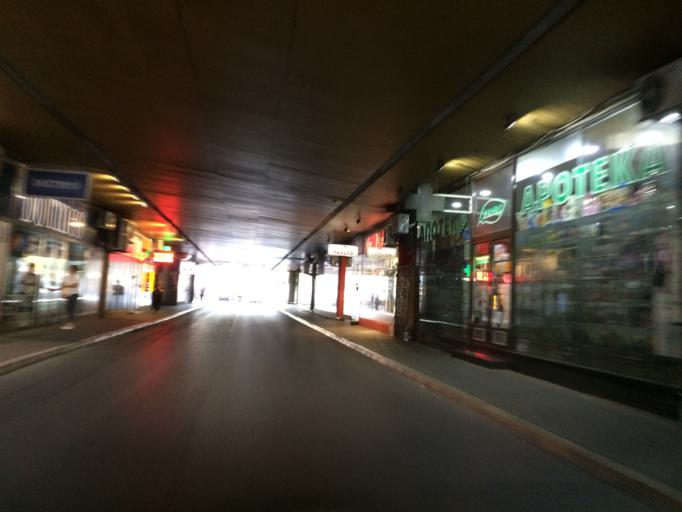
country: RS
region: Autonomna Pokrajina Vojvodina
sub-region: Juznobacki Okrug
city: Novi Sad
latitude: 45.2479
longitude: 19.8461
